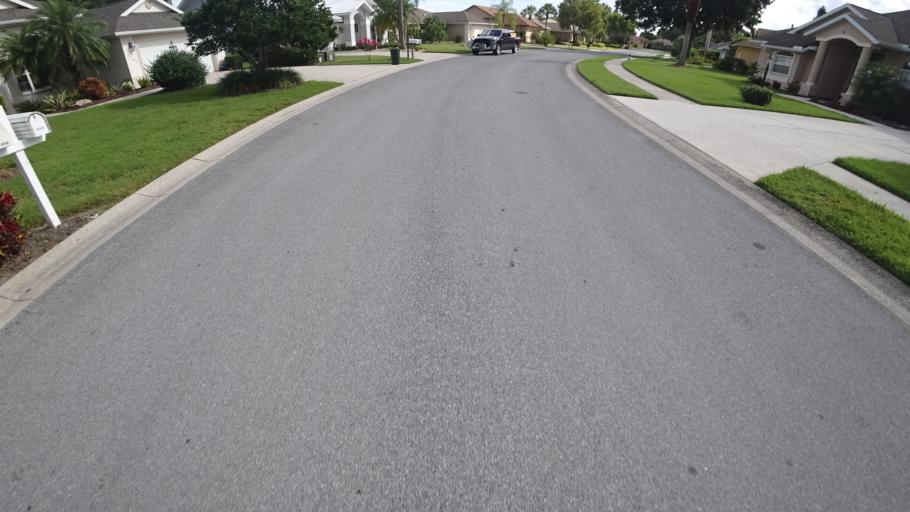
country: US
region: Florida
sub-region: Sarasota County
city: Desoto Lakes
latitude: 27.4165
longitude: -82.4886
